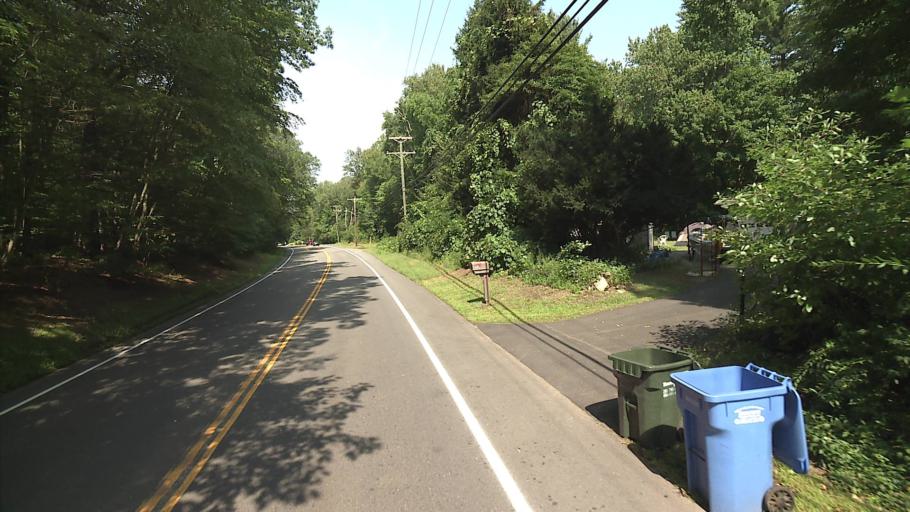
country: US
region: Connecticut
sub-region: New Haven County
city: Madison Center
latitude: 41.3207
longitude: -72.6094
